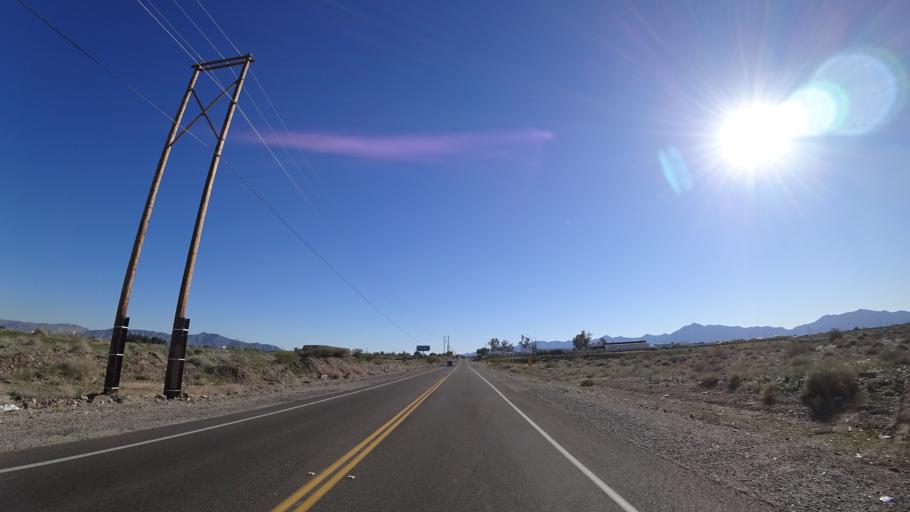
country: US
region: Arizona
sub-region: Maricopa County
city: Laveen
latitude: 33.3973
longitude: -112.2036
